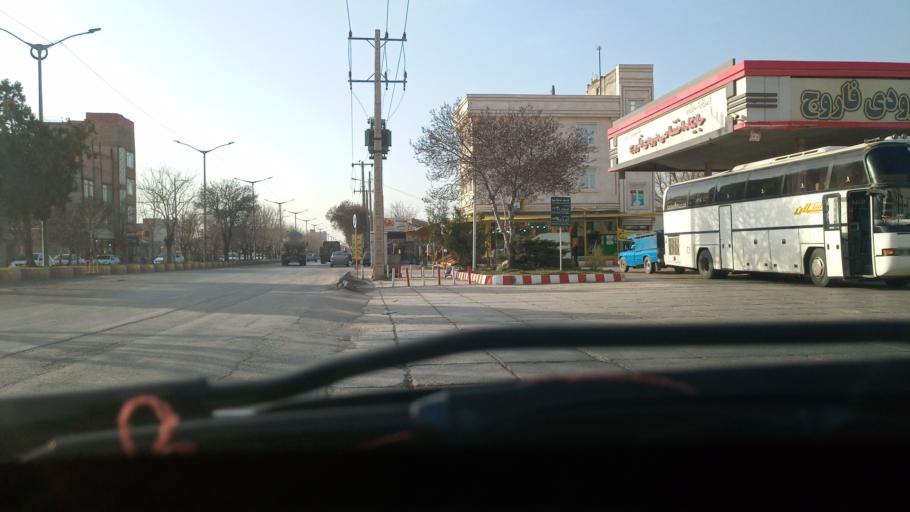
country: IR
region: Khorasan-e Shomali
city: Faruj
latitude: 37.2300
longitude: 58.2226
